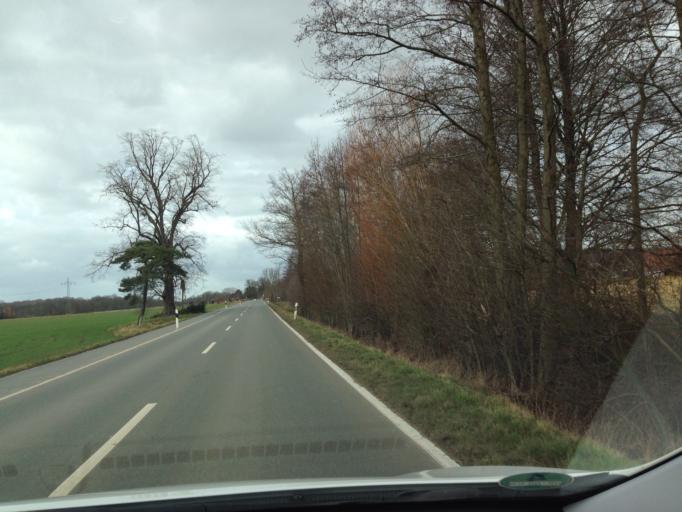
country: DE
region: North Rhine-Westphalia
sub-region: Regierungsbezirk Munster
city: Greven
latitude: 52.0314
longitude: 7.5970
